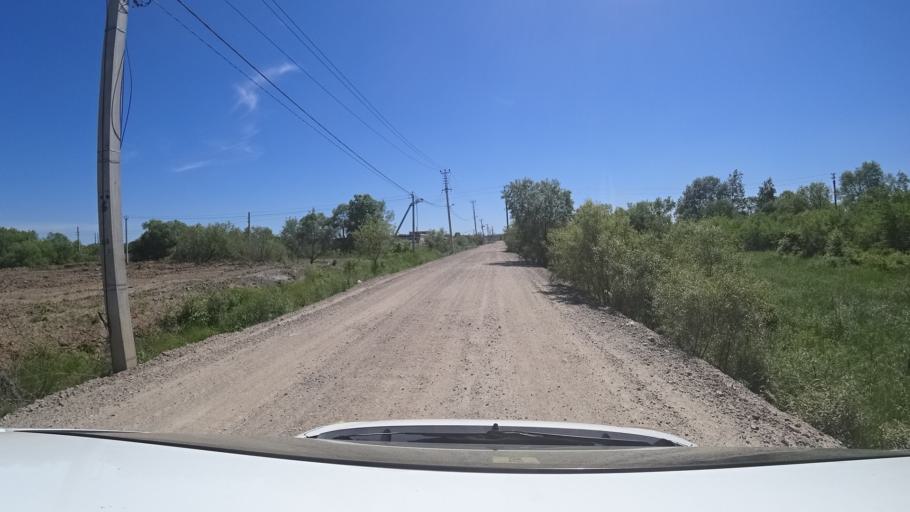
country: RU
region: Khabarovsk Krai
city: Topolevo
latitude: 48.4790
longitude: 135.1731
